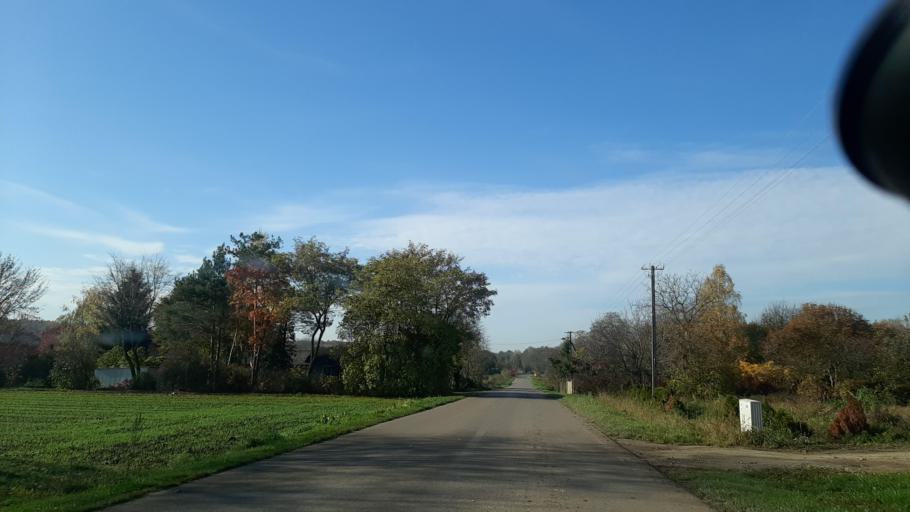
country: PL
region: Lublin Voivodeship
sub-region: Powiat lubelski
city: Jastkow
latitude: 51.3426
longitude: 22.4712
